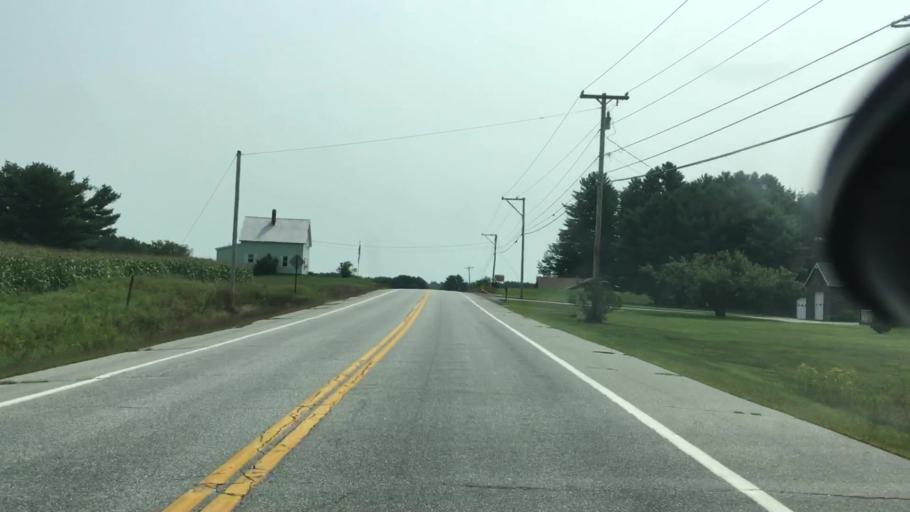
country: US
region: Maine
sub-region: Androscoggin County
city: Livermore Falls
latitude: 44.4121
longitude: -70.1423
